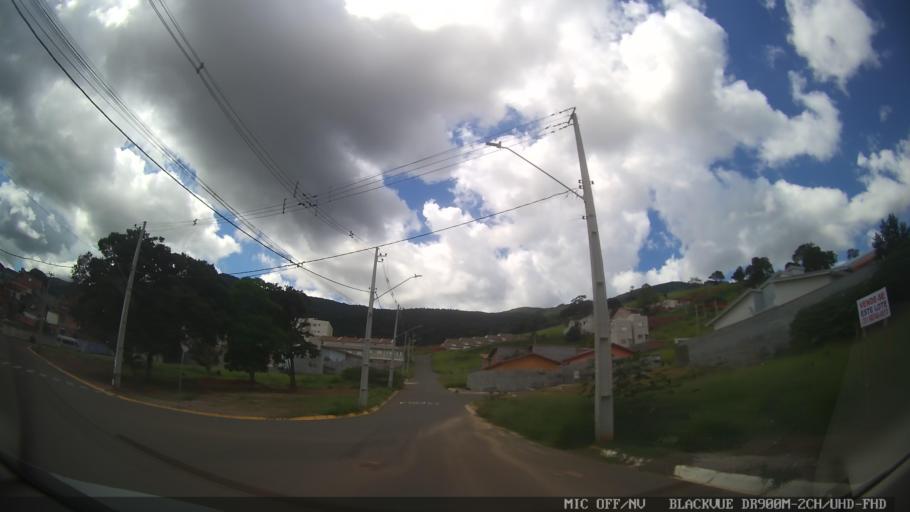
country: BR
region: Minas Gerais
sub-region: Extrema
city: Extrema
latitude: -22.8656
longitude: -46.3291
